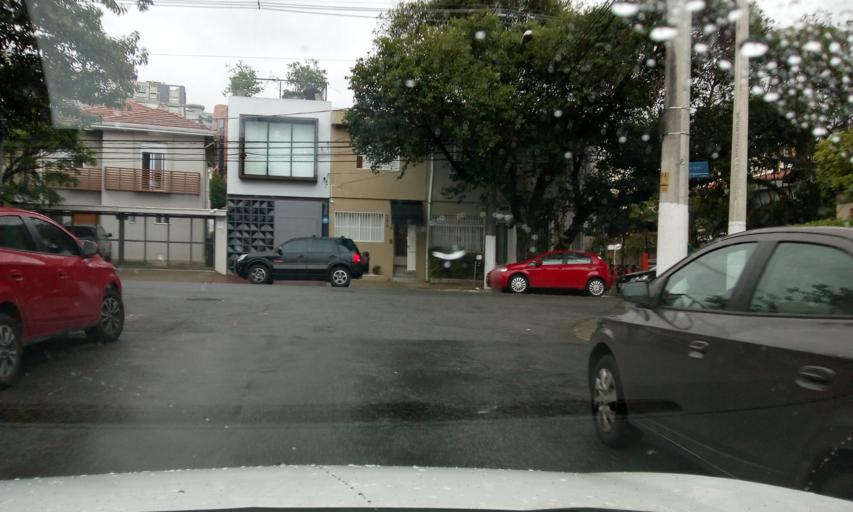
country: BR
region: Sao Paulo
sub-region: Sao Paulo
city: Sao Paulo
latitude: -23.5882
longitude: -46.6678
